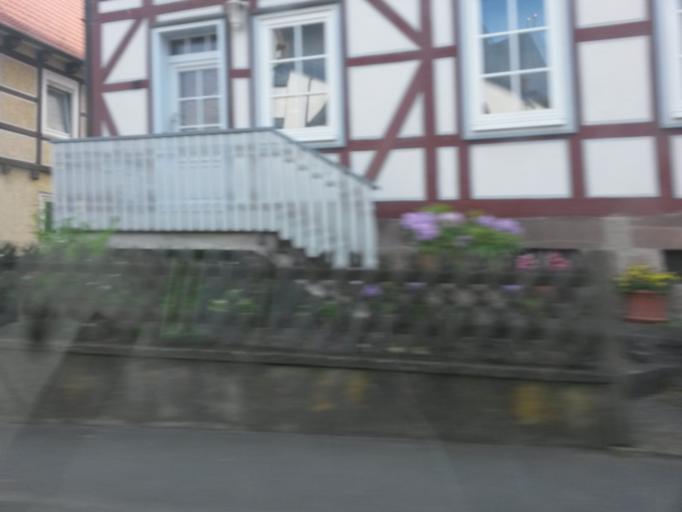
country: DE
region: Hesse
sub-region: Regierungsbezirk Kassel
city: Hilders
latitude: 50.5722
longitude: 9.9560
